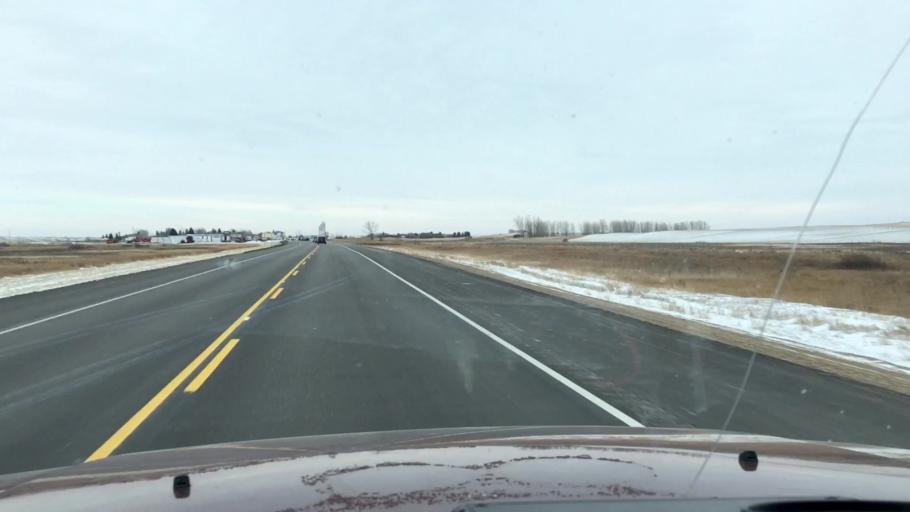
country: CA
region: Saskatchewan
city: Moose Jaw
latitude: 50.8587
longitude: -105.5834
